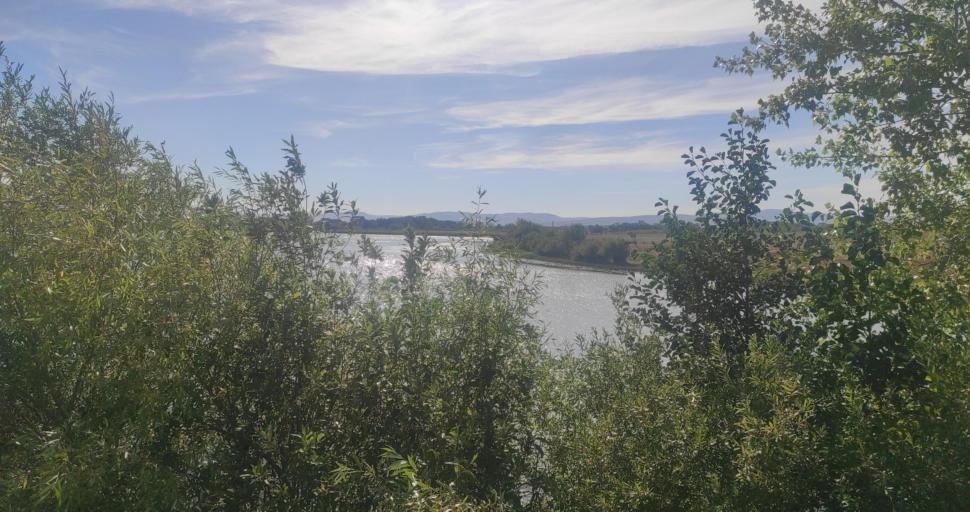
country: RU
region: Bashkortostan
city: Sibay
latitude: 52.7527
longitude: 58.6834
